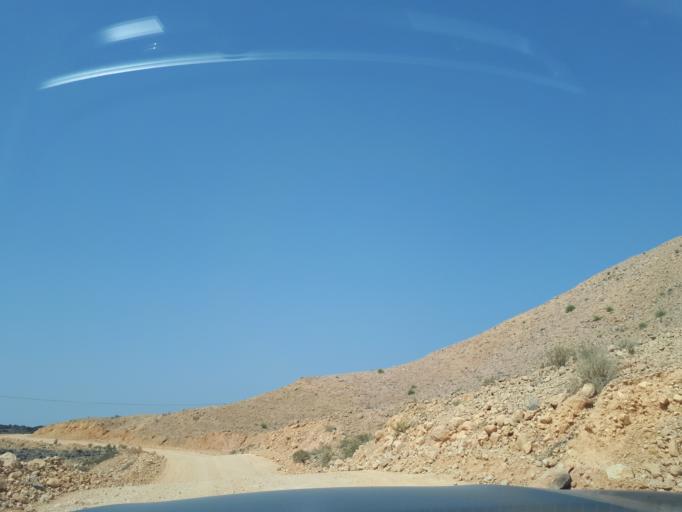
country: OM
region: Ash Sharqiyah
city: Ibra'
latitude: 23.0874
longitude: 58.9465
